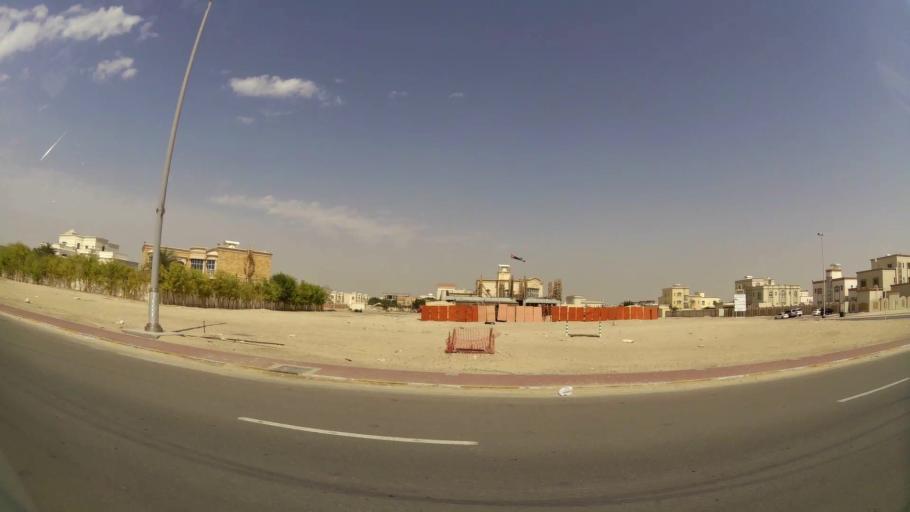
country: AE
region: Abu Dhabi
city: Abu Dhabi
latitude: 24.3070
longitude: 54.5498
